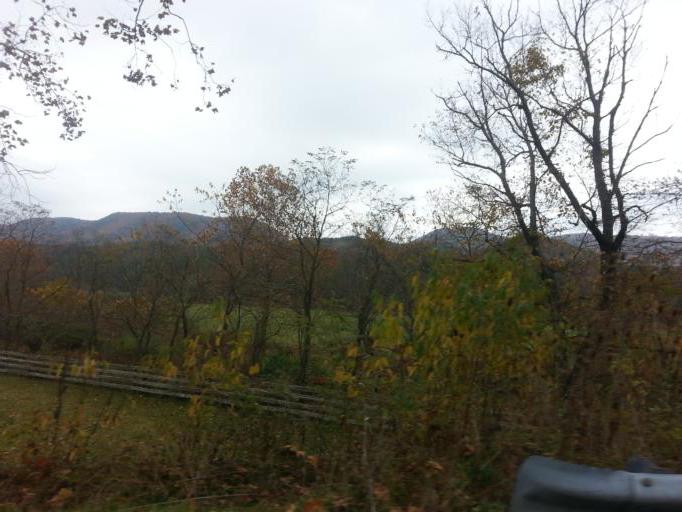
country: US
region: Virginia
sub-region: Pulaski County
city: Pulaski
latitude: 37.1020
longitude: -80.8999
